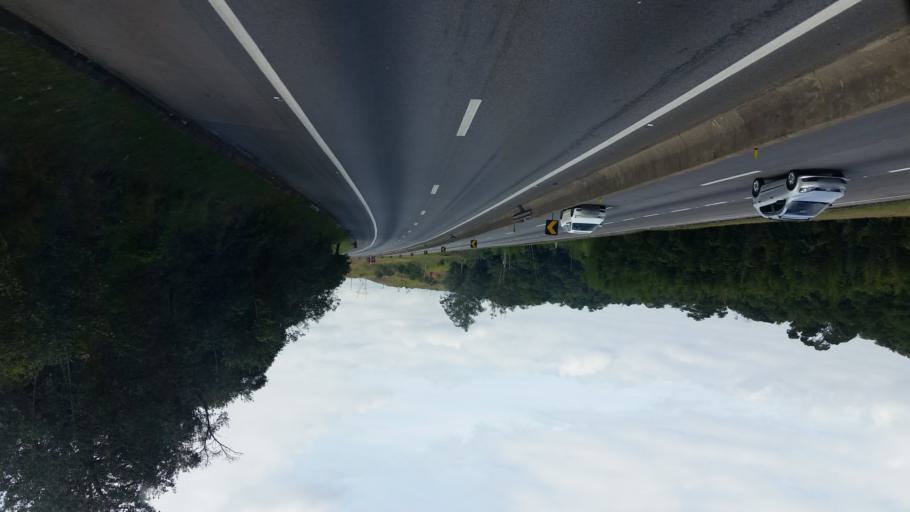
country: BR
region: Sao Paulo
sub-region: Jacarei
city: Jacarei
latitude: -23.3118
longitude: -46.0630
